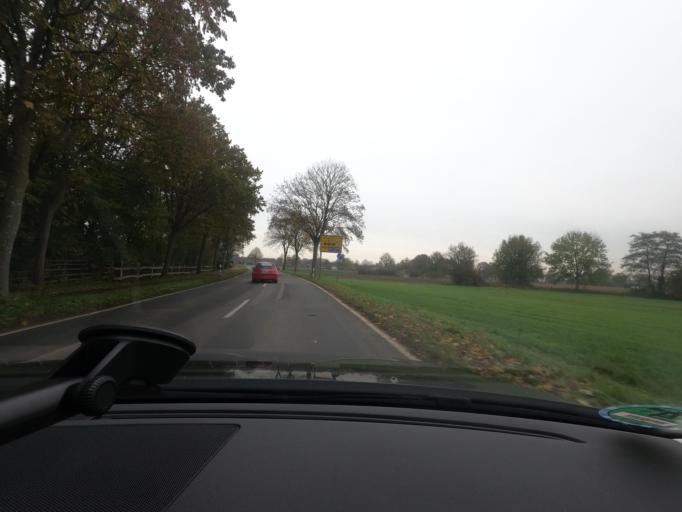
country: DE
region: North Rhine-Westphalia
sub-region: Regierungsbezirk Dusseldorf
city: Uedem
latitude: 51.6249
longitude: 6.2804
